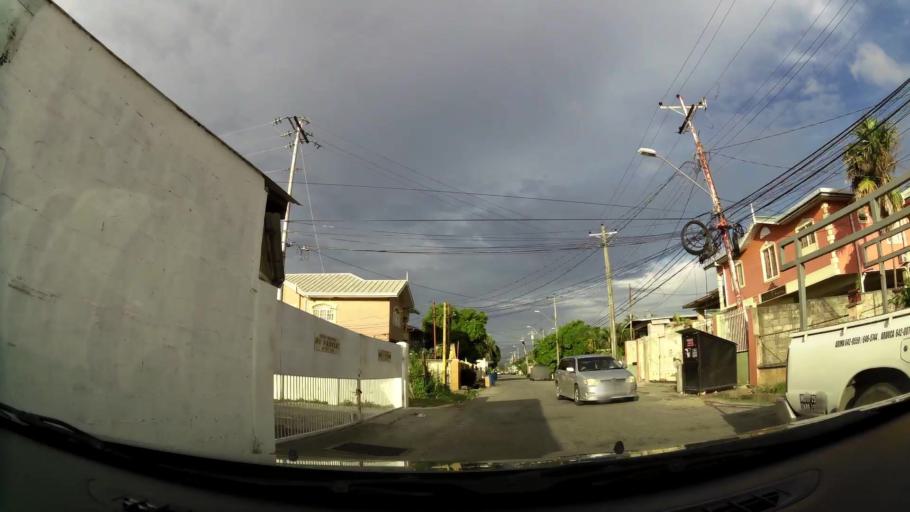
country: TT
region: Tunapuna/Piarco
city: Tunapuna
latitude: 10.6424
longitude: -61.4044
